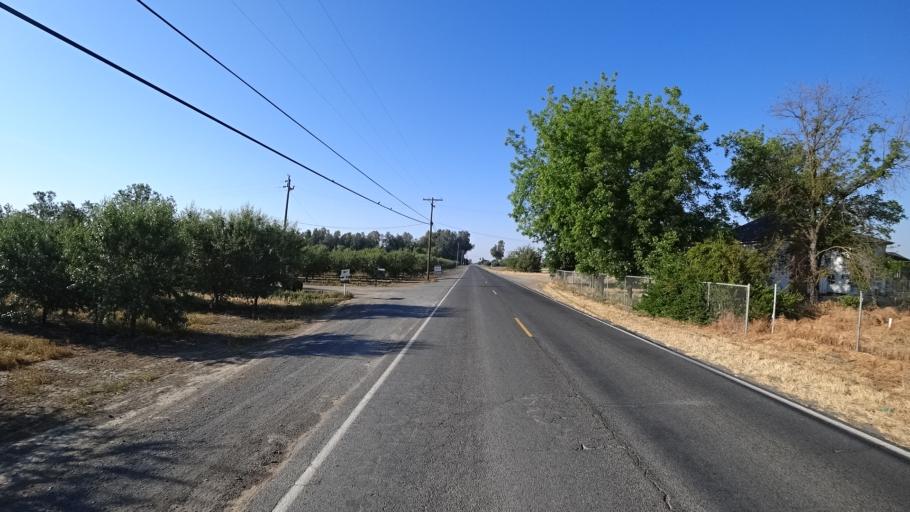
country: US
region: California
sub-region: Kings County
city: Armona
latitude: 36.2716
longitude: -119.7090
